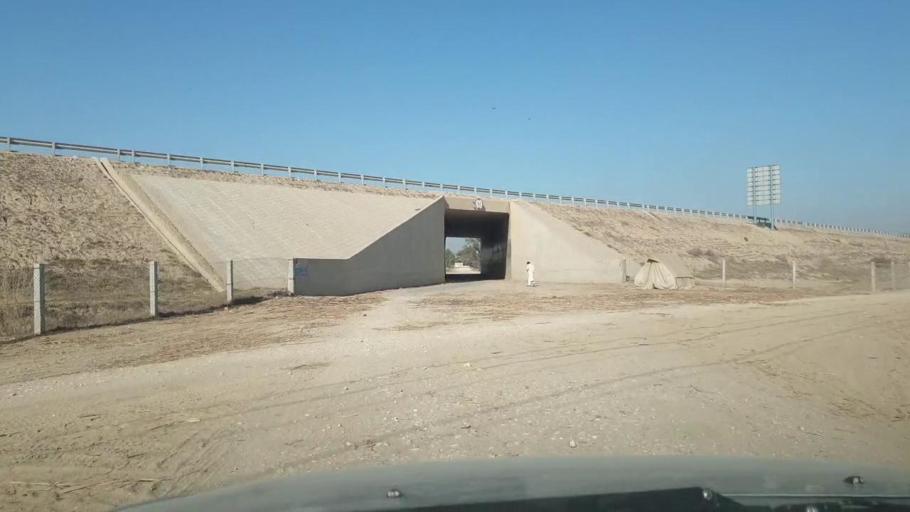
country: PK
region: Sindh
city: Ghotki
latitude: 28.0535
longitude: 69.3385
